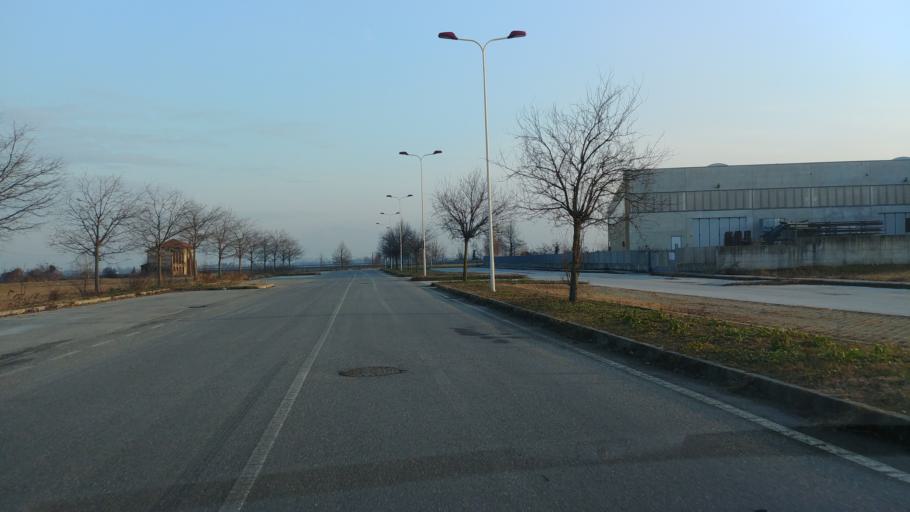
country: IT
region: Piedmont
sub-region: Provincia di Cuneo
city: Cuneo
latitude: 44.4257
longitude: 7.5654
